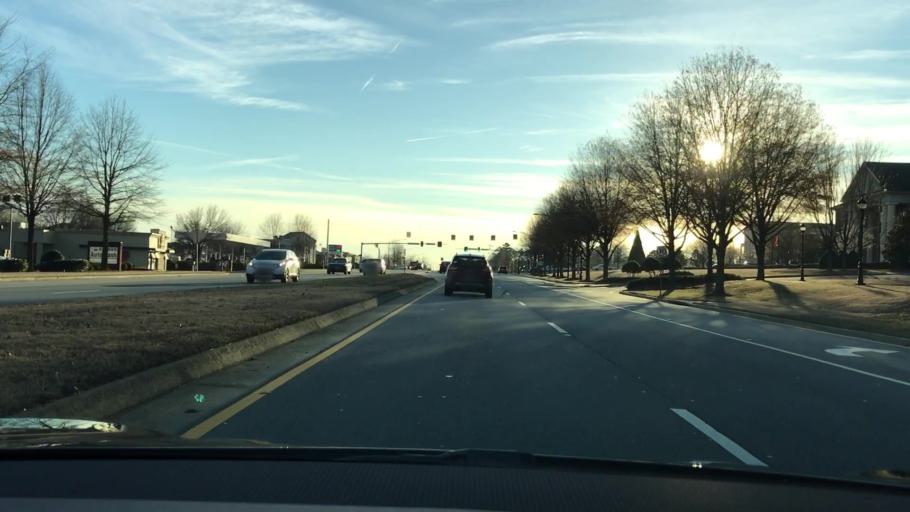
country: US
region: Georgia
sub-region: Gwinnett County
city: Buford
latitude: 34.1164
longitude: -83.9932
